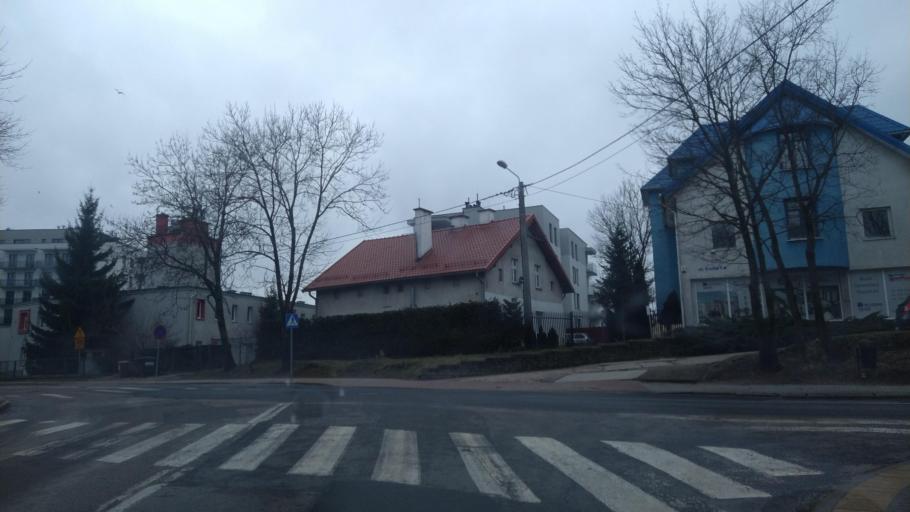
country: PL
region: Warmian-Masurian Voivodeship
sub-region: Powiat olsztynski
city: Olsztyn
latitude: 53.7894
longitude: 20.5005
